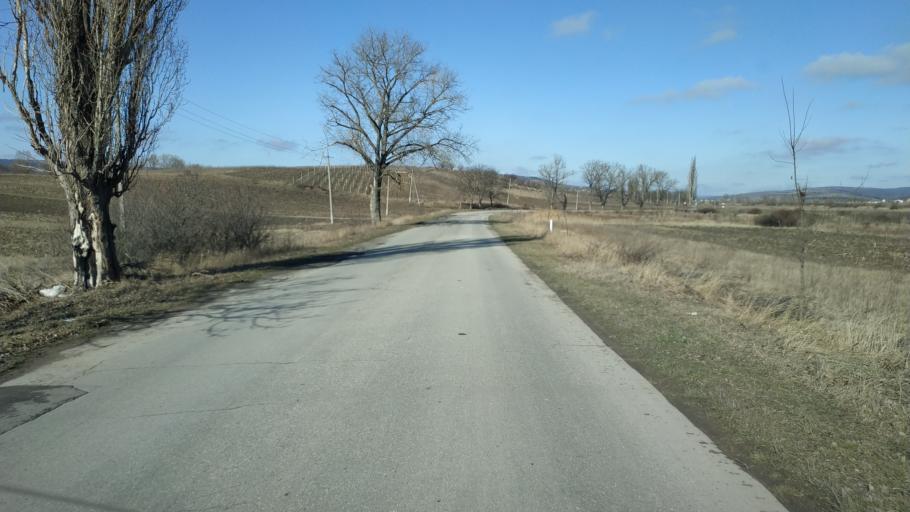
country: MD
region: Hincesti
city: Hincesti
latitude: 46.9413
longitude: 28.6271
